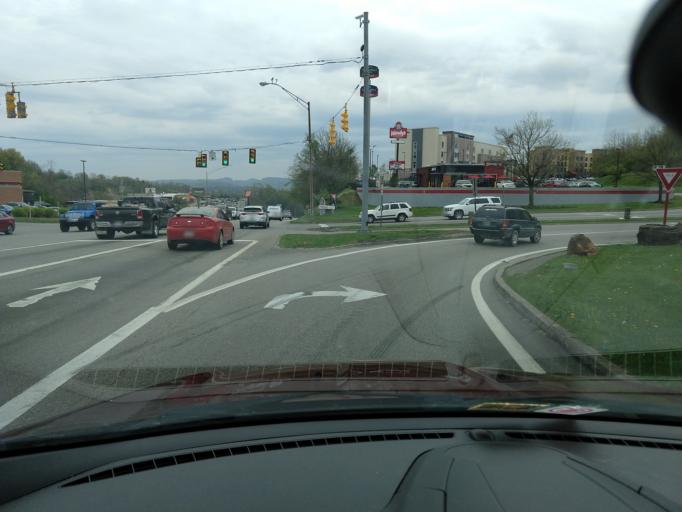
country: US
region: West Virginia
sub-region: Harrison County
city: Bridgeport
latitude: 39.2807
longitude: -80.2783
